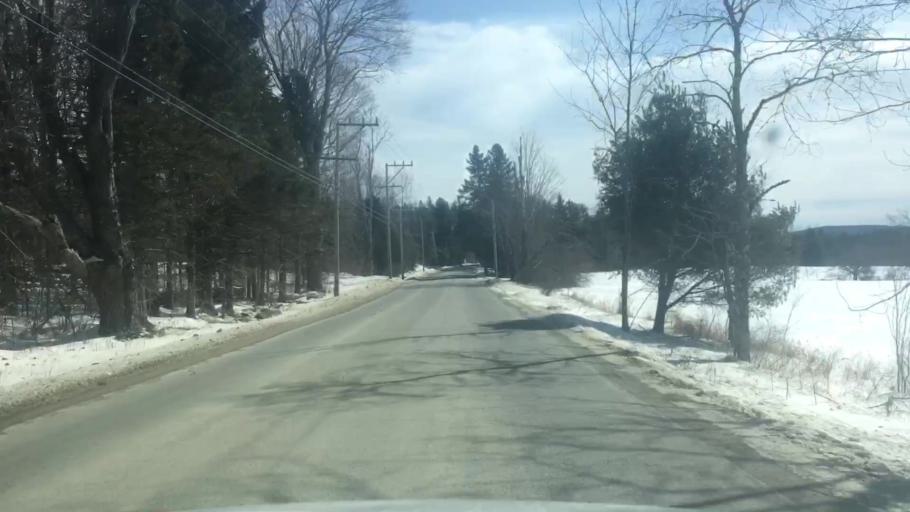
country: US
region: Maine
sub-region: Penobscot County
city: Holden
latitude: 44.7552
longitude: -68.6362
